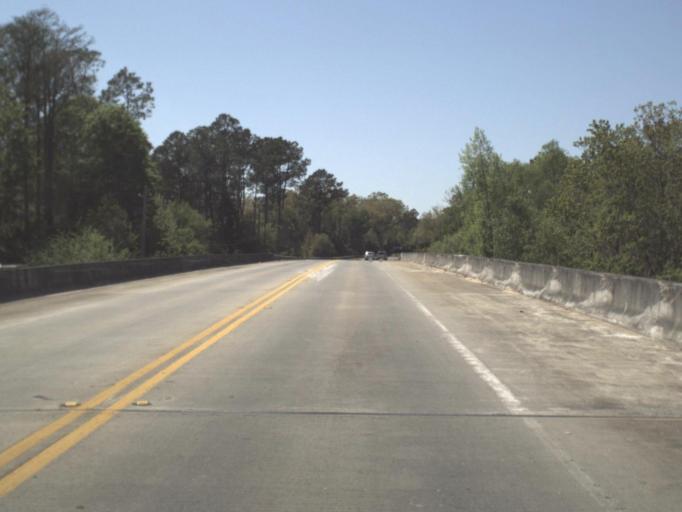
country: US
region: Florida
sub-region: Escambia County
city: Bellview
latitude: 30.4981
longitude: -87.3353
